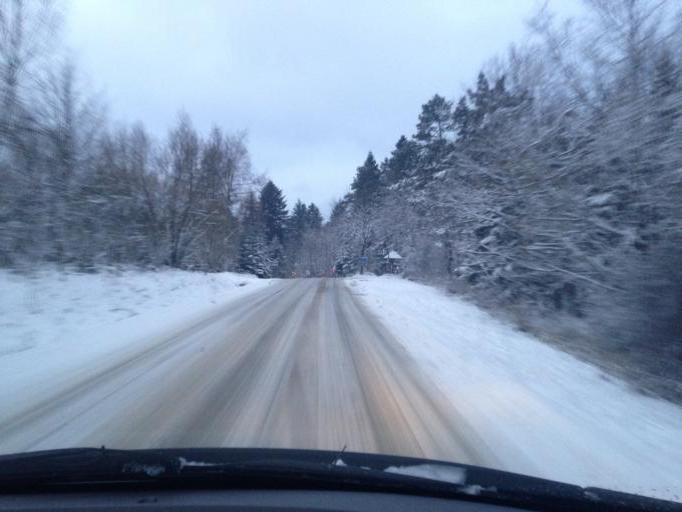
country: PL
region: Subcarpathian Voivodeship
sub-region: Powiat jasielski
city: Krempna
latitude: 49.5339
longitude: 21.4990
